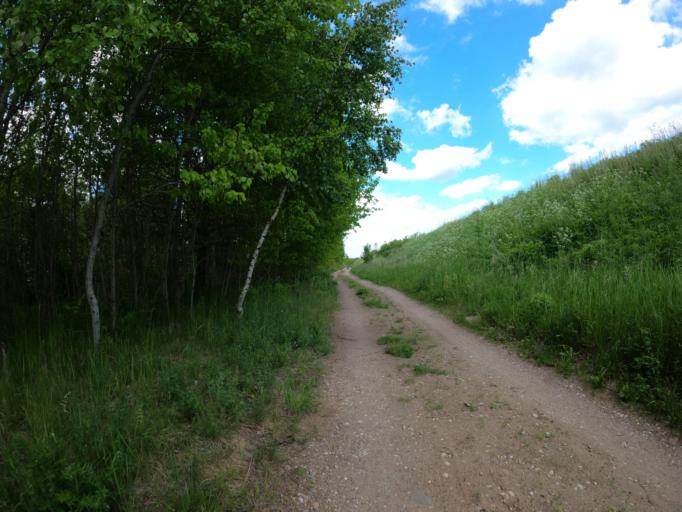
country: PL
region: Warmian-Masurian Voivodeship
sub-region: Powiat lidzbarski
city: Lidzbark Warminski
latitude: 54.1370
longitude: 20.5968
